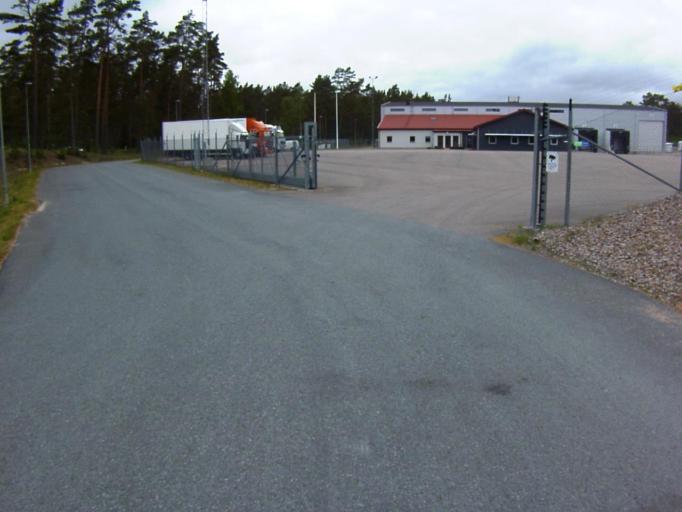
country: SE
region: Skane
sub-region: Kristianstads Kommun
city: Ahus
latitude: 55.9503
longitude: 14.2843
